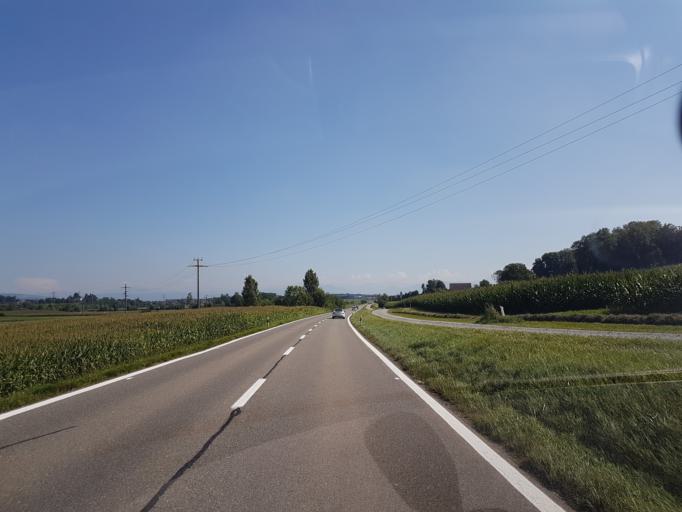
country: CH
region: Aargau
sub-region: Bezirk Muri
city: Waltenschwil
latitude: 47.3206
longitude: 8.3007
